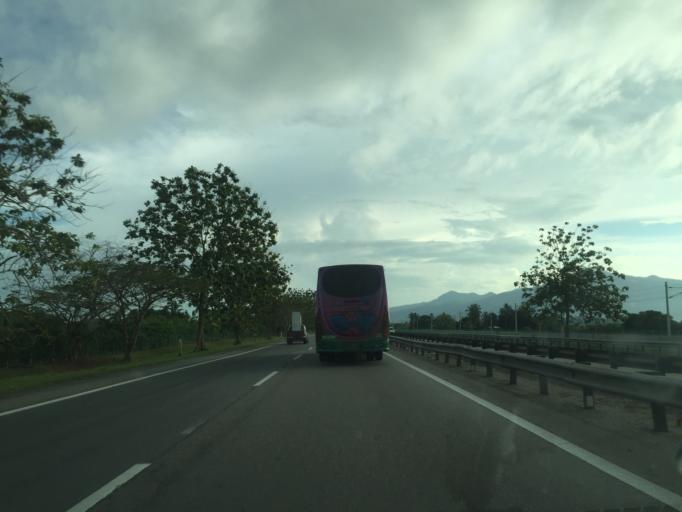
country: MY
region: Kedah
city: Gurun
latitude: 5.8897
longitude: 100.4774
